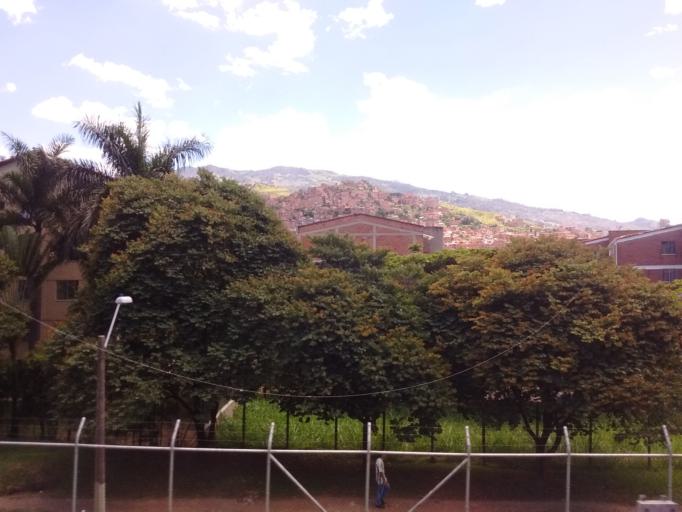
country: CO
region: Antioquia
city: Medellin
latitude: 6.2560
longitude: -75.6113
